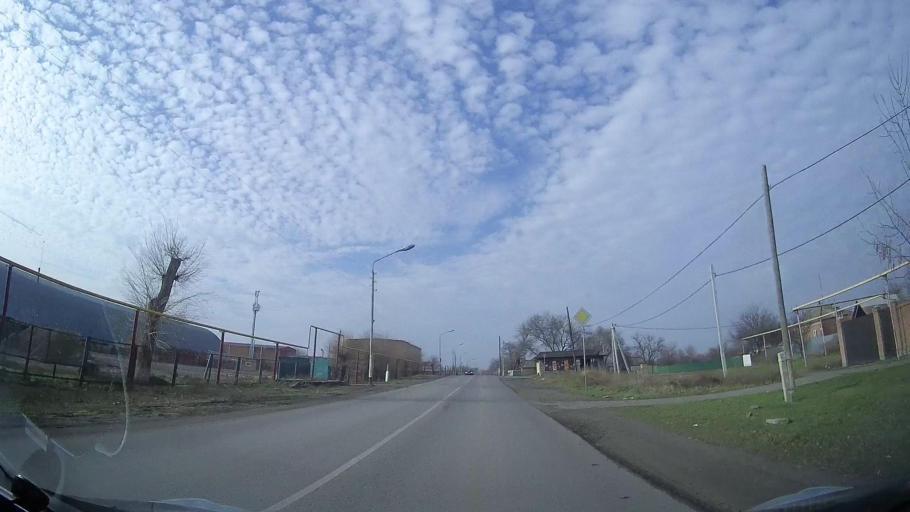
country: RU
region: Rostov
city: Veselyy
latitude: 47.0872
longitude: 40.7568
